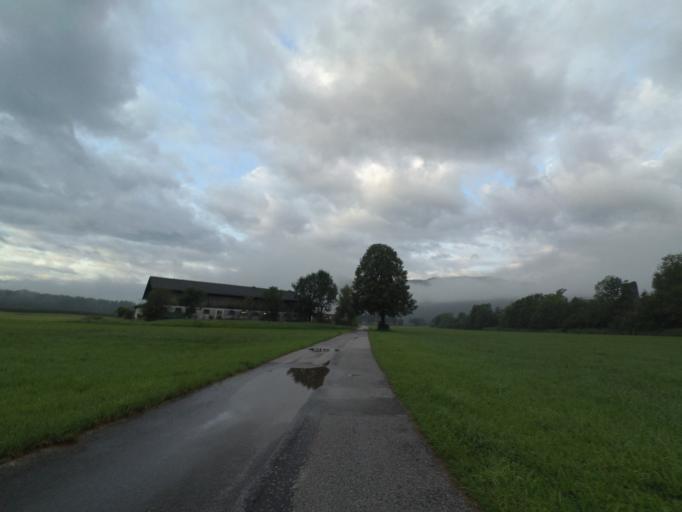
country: AT
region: Salzburg
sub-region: Politischer Bezirk Hallein
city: Puch bei Hallein
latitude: 47.7222
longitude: 13.0745
